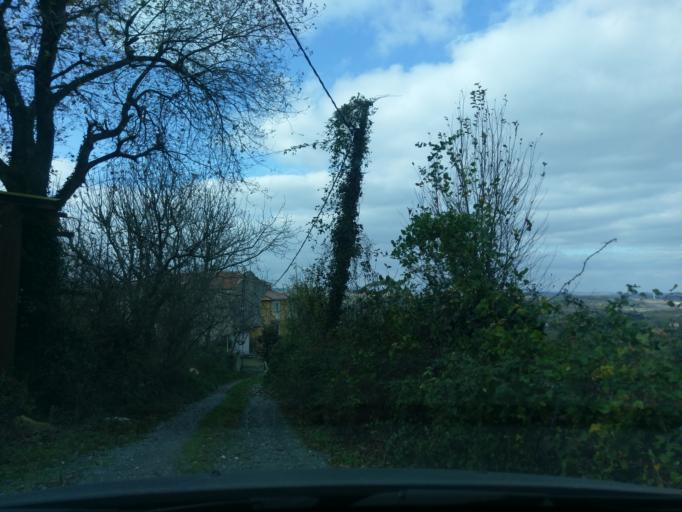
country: TR
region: Istanbul
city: Durusu
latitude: 41.2765
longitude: 28.6973
